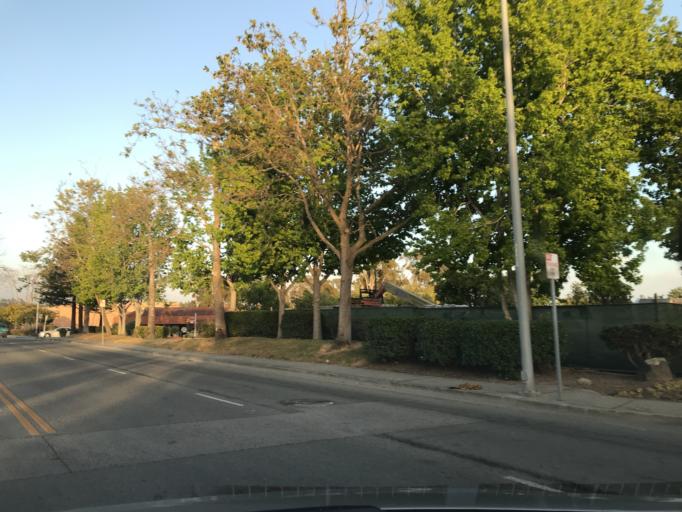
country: US
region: California
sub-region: Santa Cruz County
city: Live Oak
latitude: 36.9783
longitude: -121.9686
